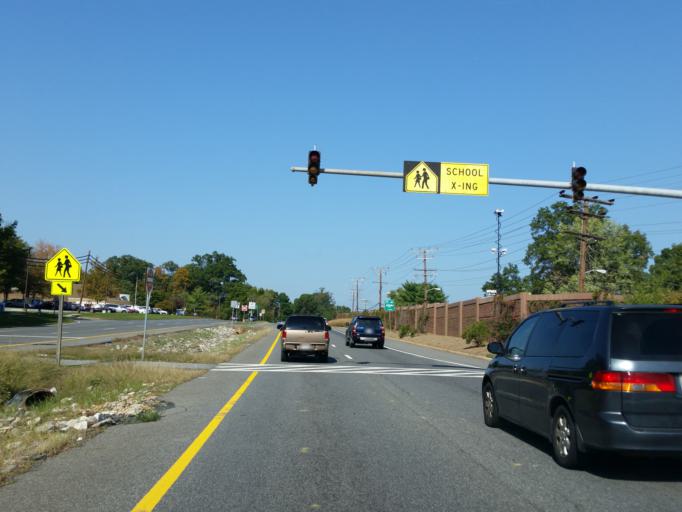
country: US
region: Maryland
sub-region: Prince George's County
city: South Laurel
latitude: 39.0709
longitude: -76.8441
